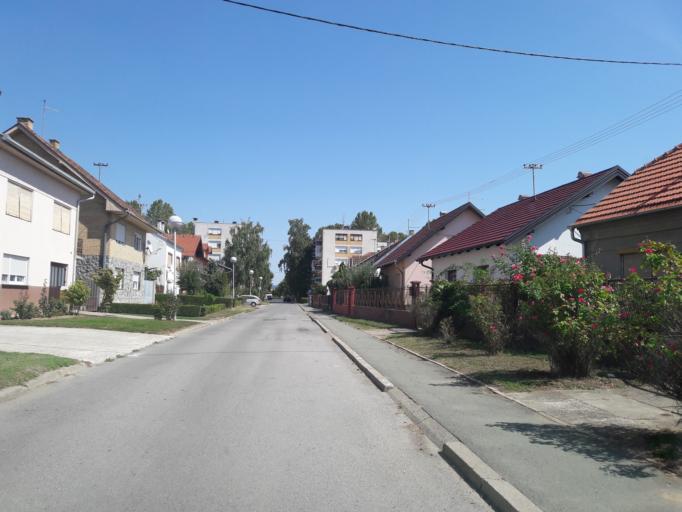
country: HR
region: Osjecko-Baranjska
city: Visnjevac
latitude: 45.5624
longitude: 18.6511
